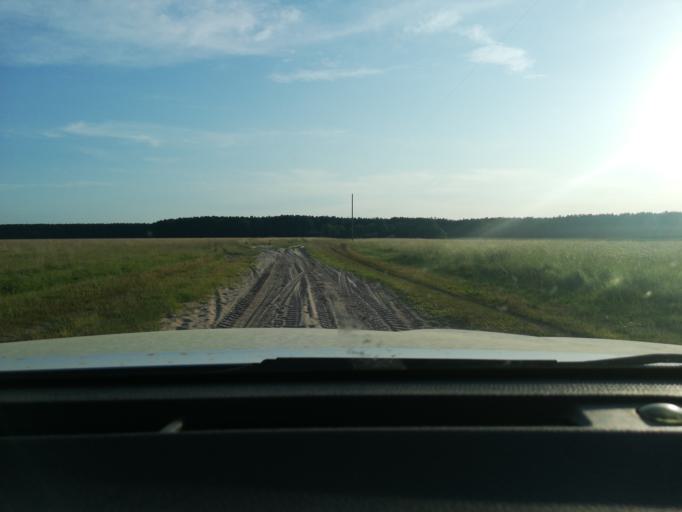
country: AR
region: Corrientes
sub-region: Departamento de San Miguel
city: San Miguel
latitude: -27.9976
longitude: -57.5258
